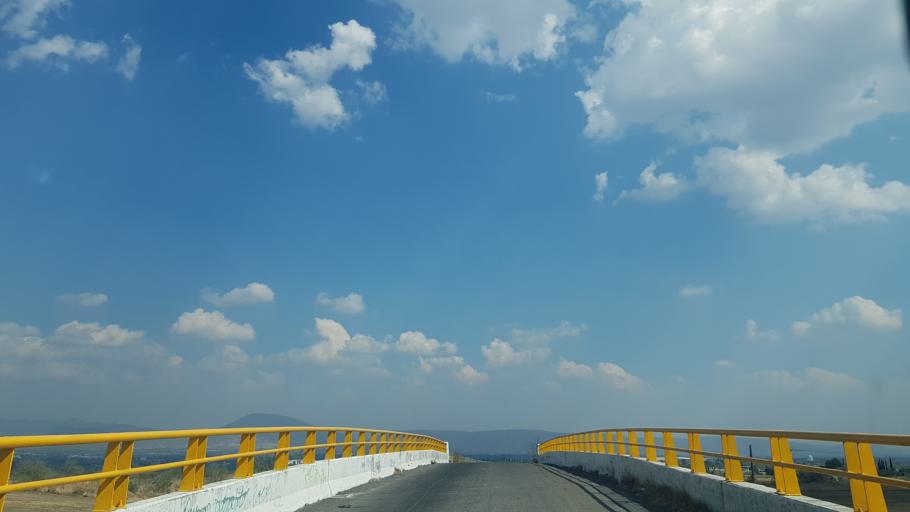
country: MX
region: Puebla
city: Atlixco
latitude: 18.9207
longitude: -98.4829
